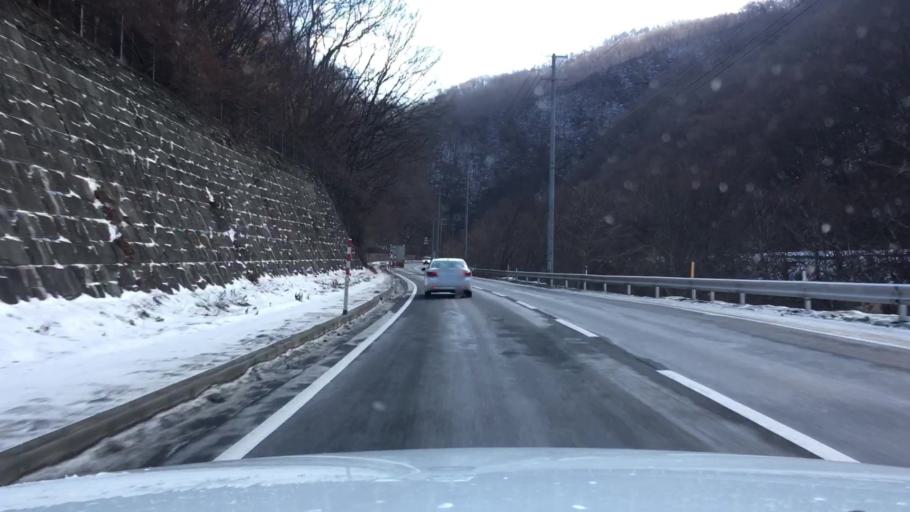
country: JP
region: Iwate
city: Tono
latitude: 39.6445
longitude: 141.5490
